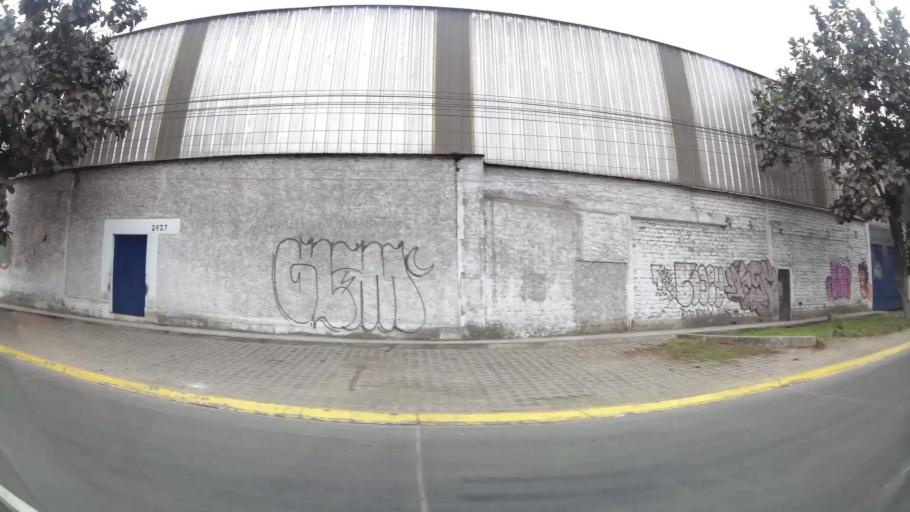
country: PE
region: Callao
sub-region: Callao
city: Callao
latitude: -12.0501
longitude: -77.1178
